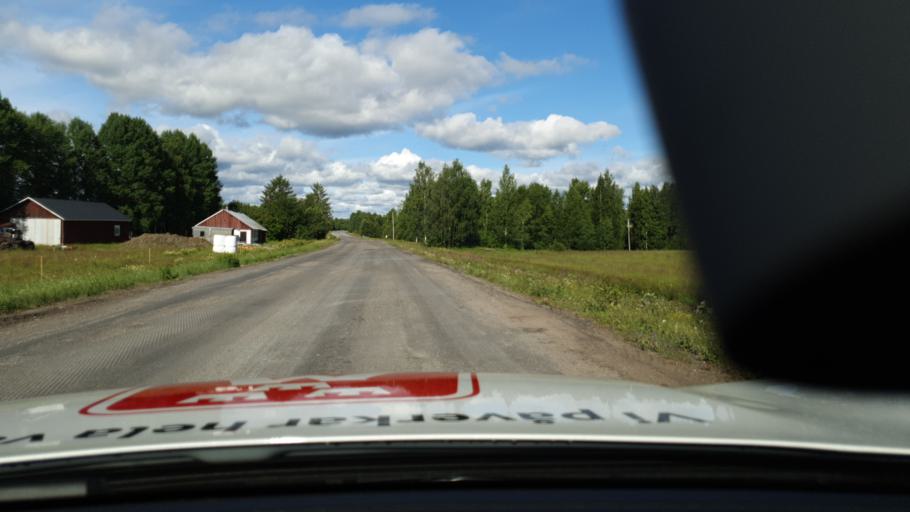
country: SE
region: Norrbotten
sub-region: Bodens Kommun
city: Boden
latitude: 65.8521
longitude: 21.5093
